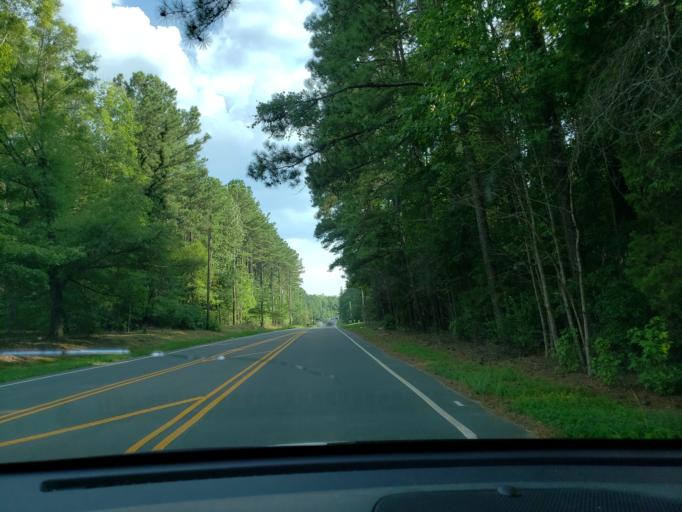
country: US
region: North Carolina
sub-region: Orange County
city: Chapel Hill
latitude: 35.8921
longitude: -78.9811
